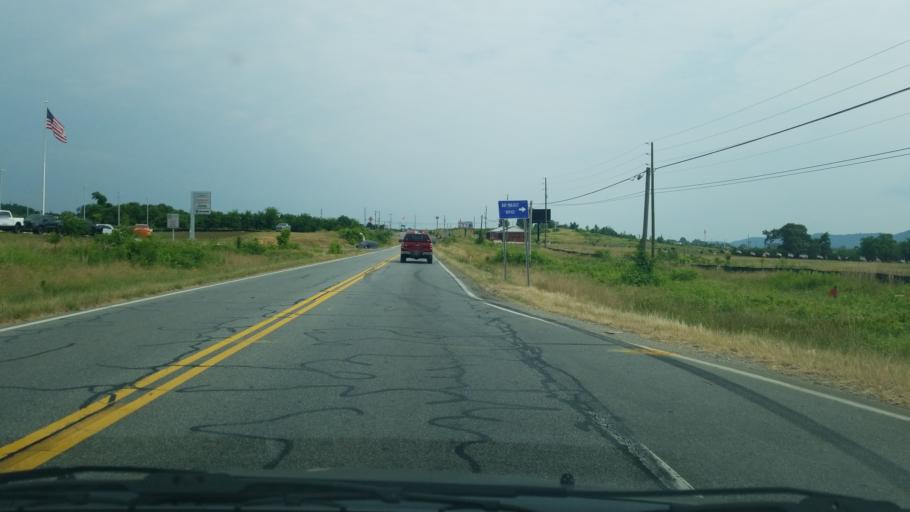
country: US
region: Georgia
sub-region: Catoosa County
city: Ringgold
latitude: 34.9003
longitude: -85.1308
